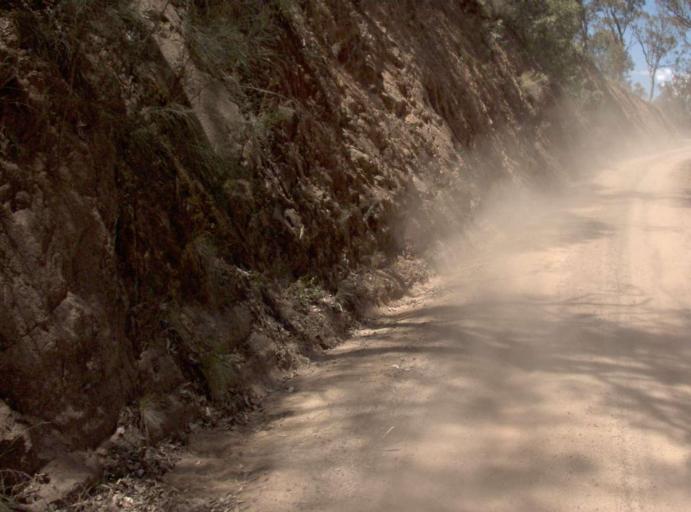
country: AU
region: New South Wales
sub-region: Snowy River
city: Jindabyne
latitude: -37.0793
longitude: 148.3604
